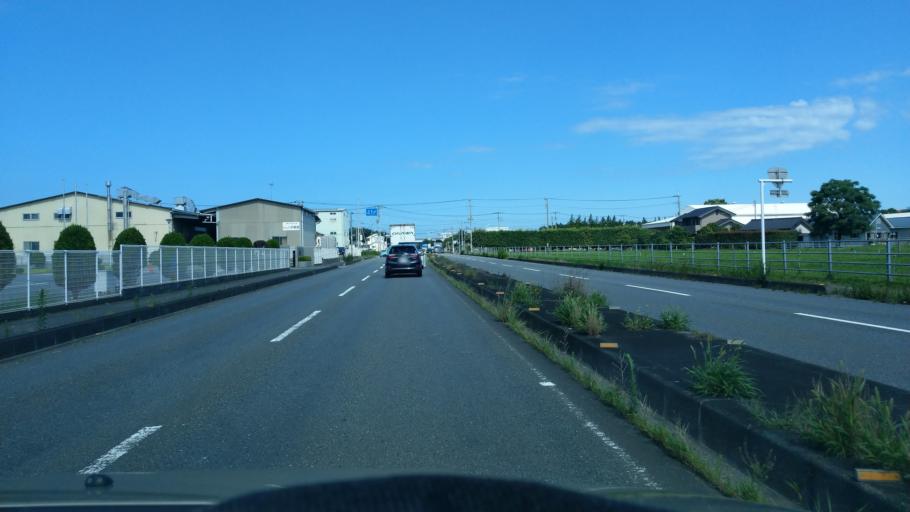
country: JP
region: Saitama
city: Sakado
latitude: 36.0369
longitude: 139.3574
